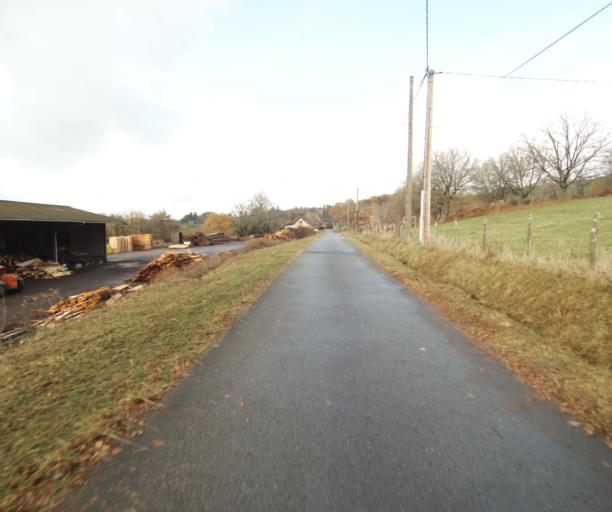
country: FR
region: Limousin
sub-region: Departement de la Correze
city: Cornil
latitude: 45.2196
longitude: 1.6610
